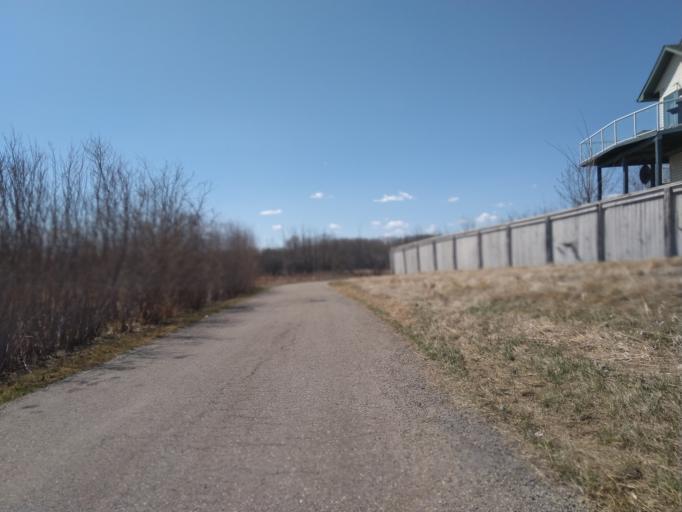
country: CA
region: Alberta
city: Chestermere
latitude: 51.0845
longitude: -113.9242
